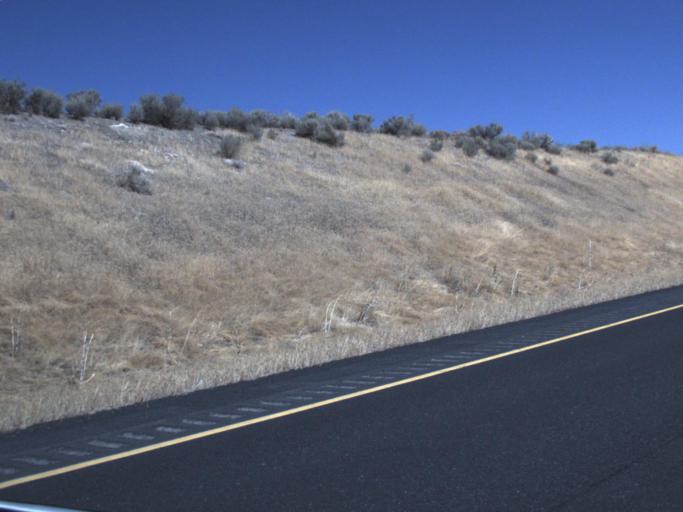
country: US
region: Washington
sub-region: Grant County
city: Warden
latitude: 47.0858
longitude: -118.8281
